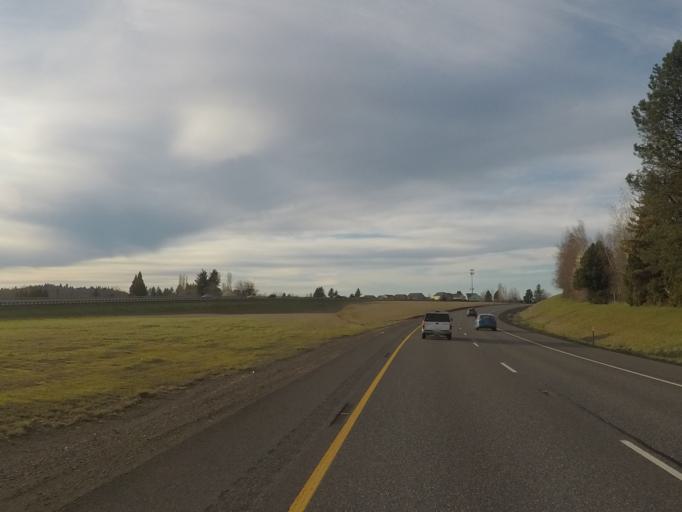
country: US
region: Oregon
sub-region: Multnomah County
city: Gresham
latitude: 45.4718
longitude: -122.3948
